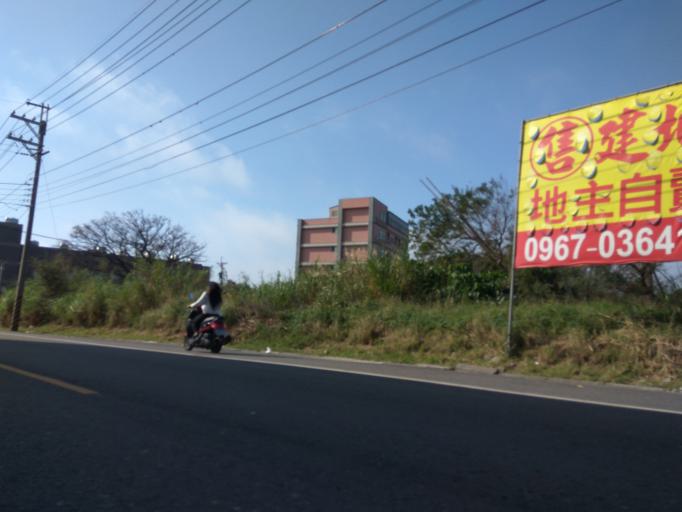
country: TW
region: Taiwan
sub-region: Hsinchu
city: Zhubei
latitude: 25.0357
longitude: 121.0777
